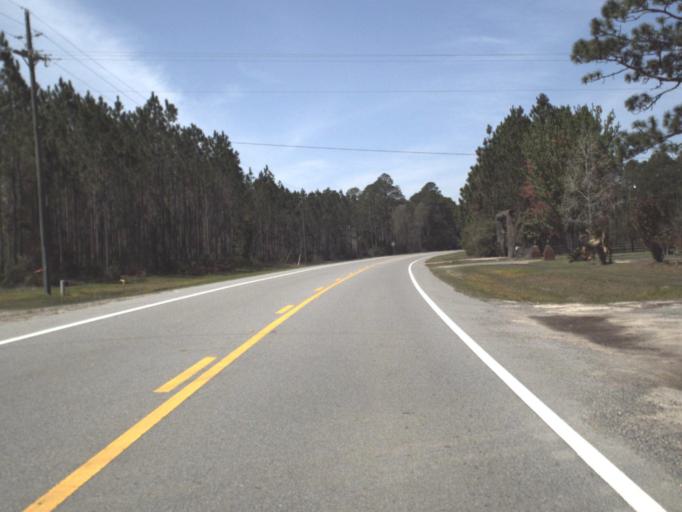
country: US
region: Florida
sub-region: Bay County
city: Lynn Haven
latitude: 30.3222
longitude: -85.6871
